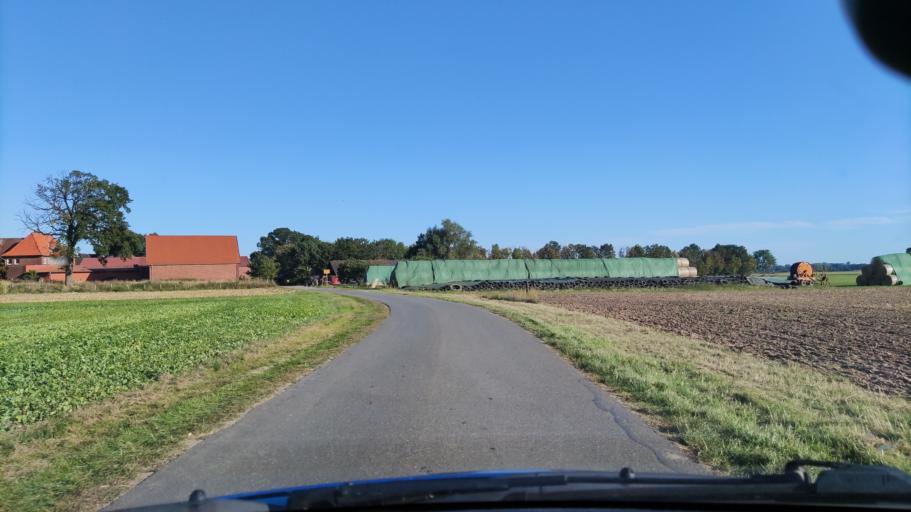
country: DE
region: Lower Saxony
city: Dannenberg
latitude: 53.1287
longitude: 11.0802
